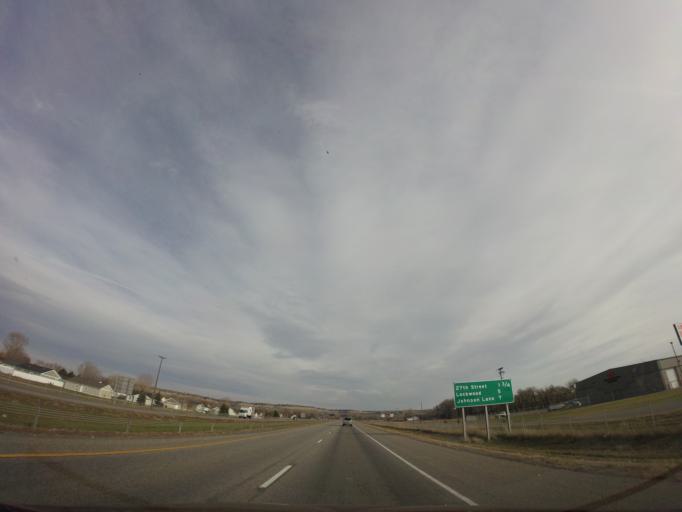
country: US
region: Montana
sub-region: Yellowstone County
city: Billings
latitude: 45.7522
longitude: -108.5164
